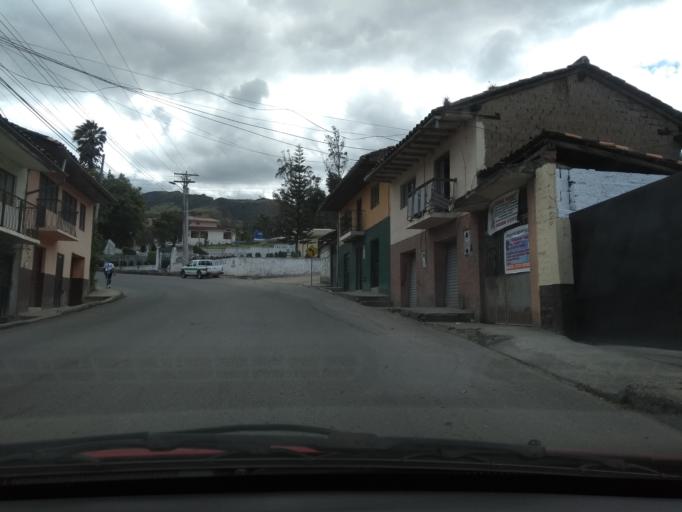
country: EC
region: Azuay
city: Cuenca
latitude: -3.1582
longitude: -79.1508
